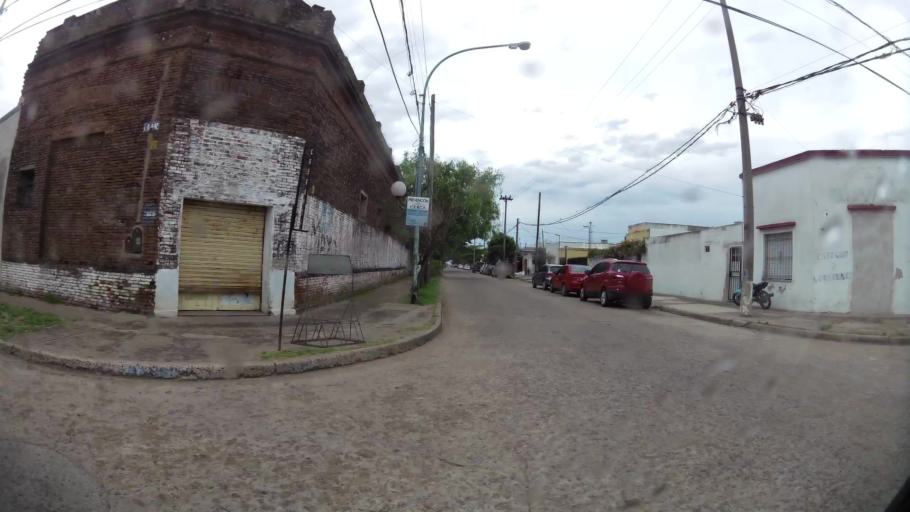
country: AR
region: Buenos Aires
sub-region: Partido de Zarate
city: Zarate
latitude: -34.0863
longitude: -59.0360
